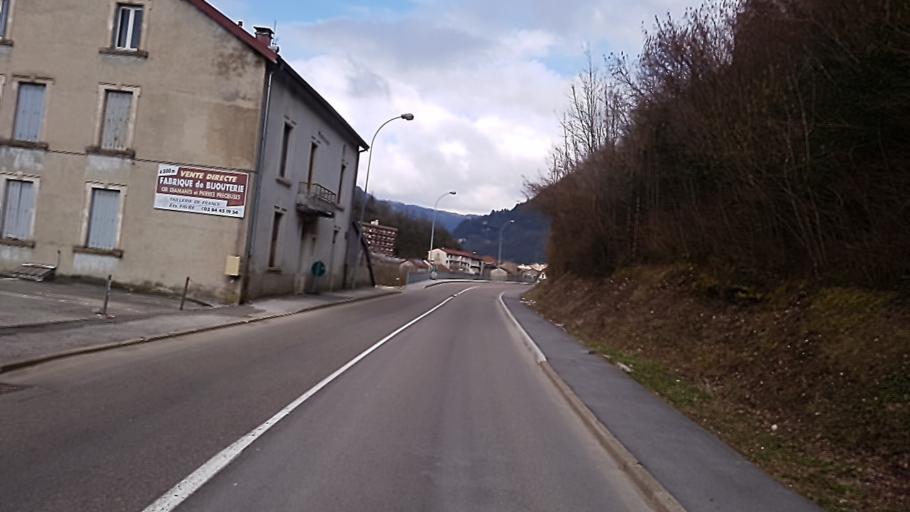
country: FR
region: Franche-Comte
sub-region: Departement du Jura
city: Saint-Claude
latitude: 46.3814
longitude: 5.8536
